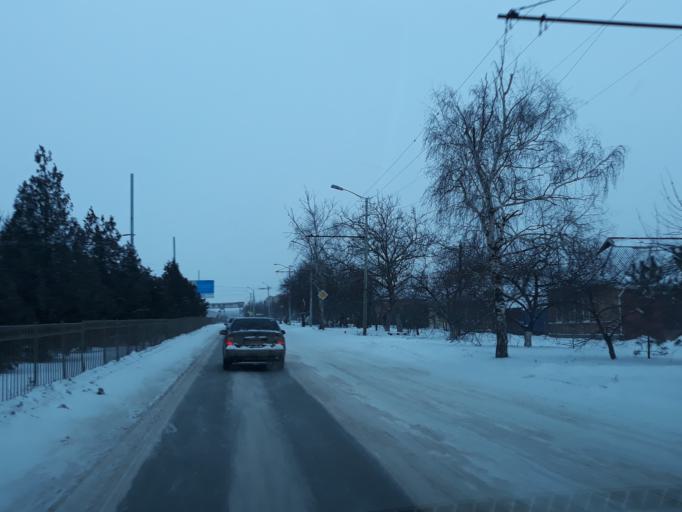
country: RU
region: Rostov
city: Taganrog
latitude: 47.2702
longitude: 38.9213
